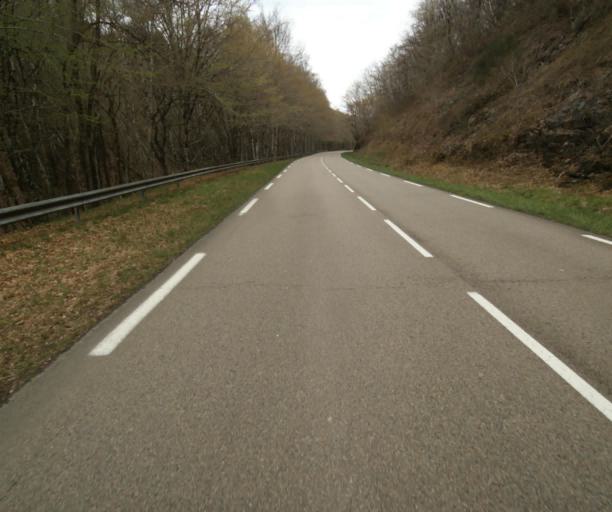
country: FR
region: Limousin
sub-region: Departement de la Correze
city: Sainte-Fortunade
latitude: 45.1869
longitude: 1.8464
